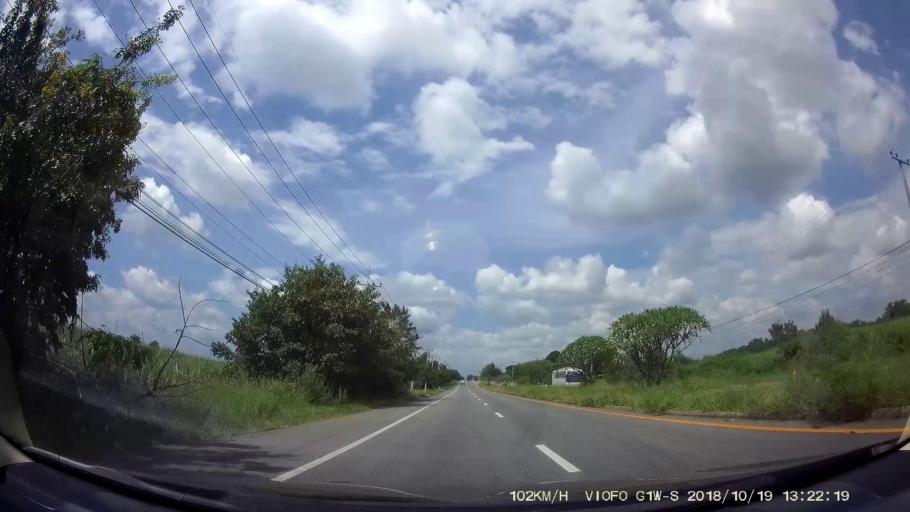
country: TH
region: Chaiyaphum
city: Chatturat
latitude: 15.4754
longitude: 101.8239
